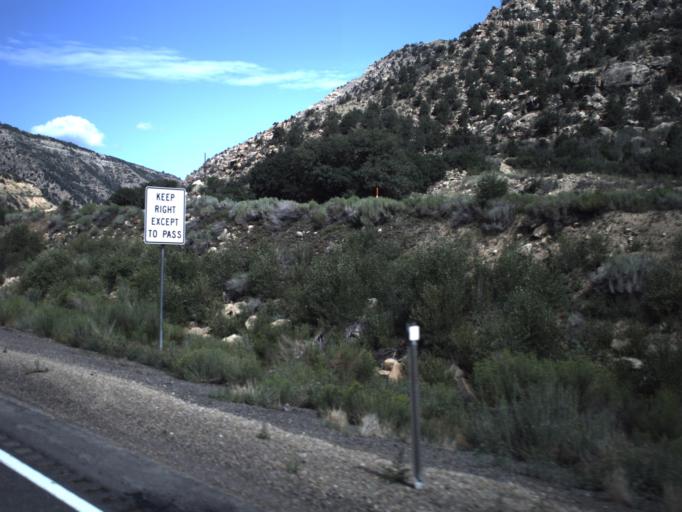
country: US
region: Utah
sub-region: Carbon County
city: Helper
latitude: 39.7764
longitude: -110.9139
